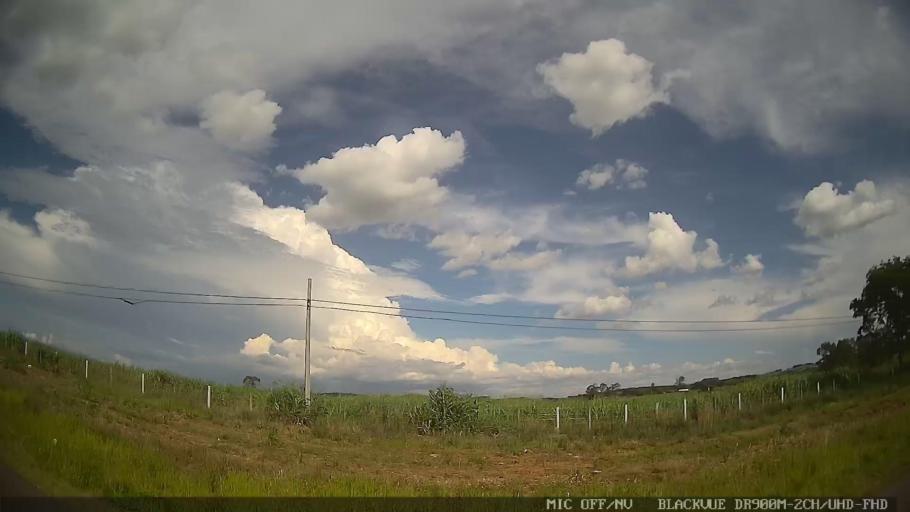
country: BR
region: Sao Paulo
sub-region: Conchas
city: Conchas
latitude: -23.0515
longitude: -47.9588
